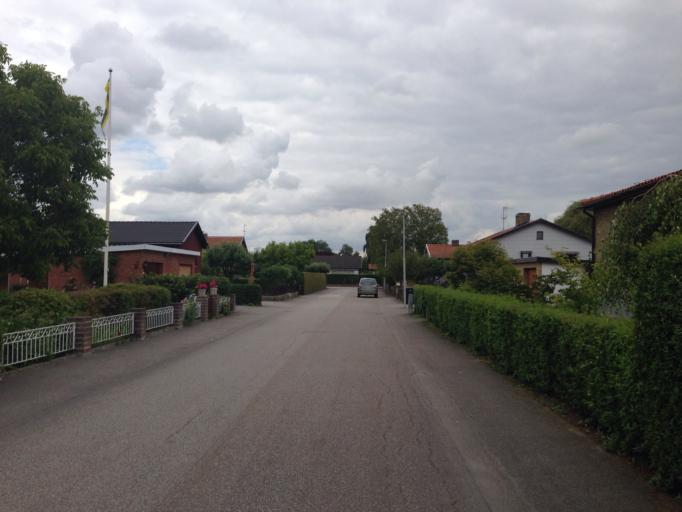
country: SE
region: Skane
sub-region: Lomma Kommun
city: Lomma
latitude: 55.6758
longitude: 13.0788
